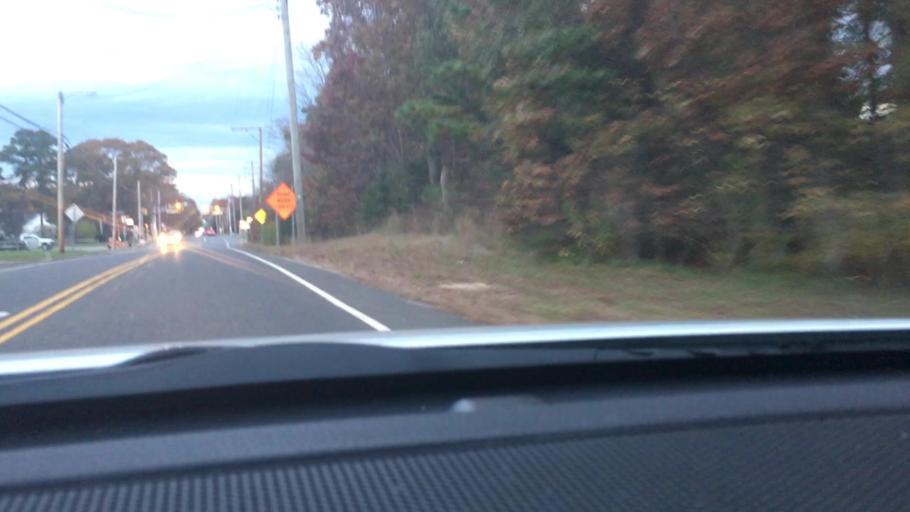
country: US
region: New Jersey
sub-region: Atlantic County
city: Absecon
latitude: 39.4381
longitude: -74.4983
